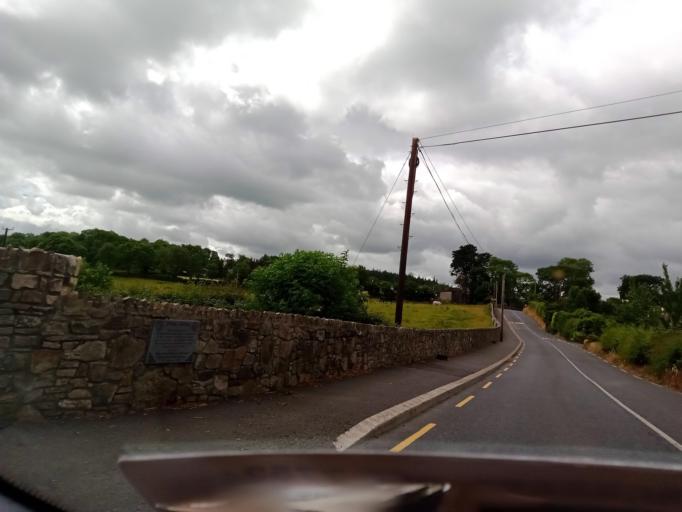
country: IE
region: Leinster
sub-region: Kilkenny
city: Thomastown
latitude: 52.4733
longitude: -7.2616
